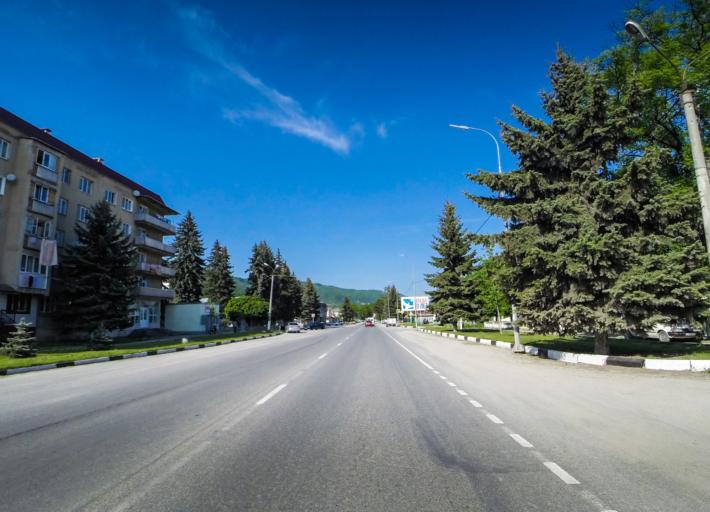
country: RU
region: Kabardino-Balkariya
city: Kashkhatau
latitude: 43.3154
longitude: 43.6042
